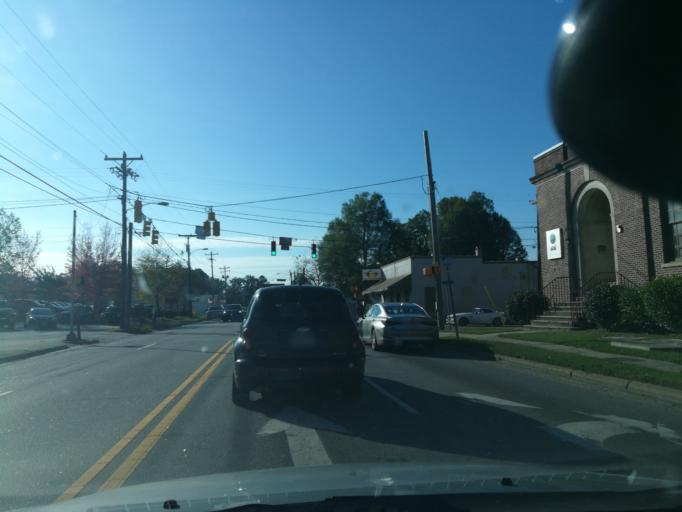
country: US
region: North Carolina
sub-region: Durham County
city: Durham
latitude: 36.0297
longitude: -78.8904
